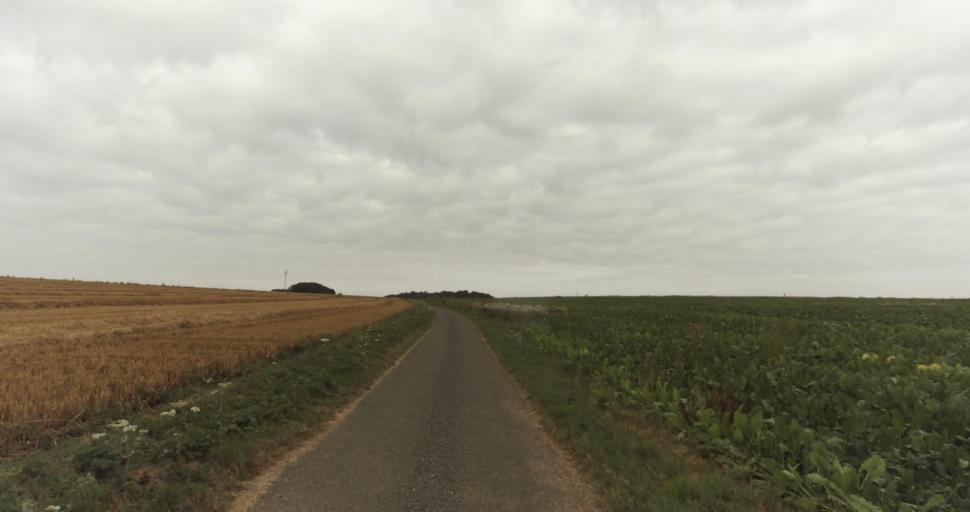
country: FR
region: Haute-Normandie
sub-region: Departement de l'Eure
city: Saint-Germain-sur-Avre
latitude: 48.8083
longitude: 1.2800
